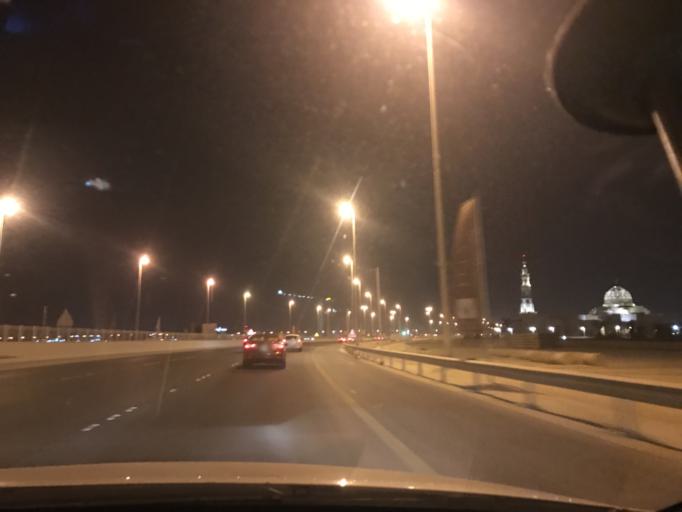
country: BH
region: Muharraq
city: Al Muharraq
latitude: 26.2979
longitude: 50.6432
